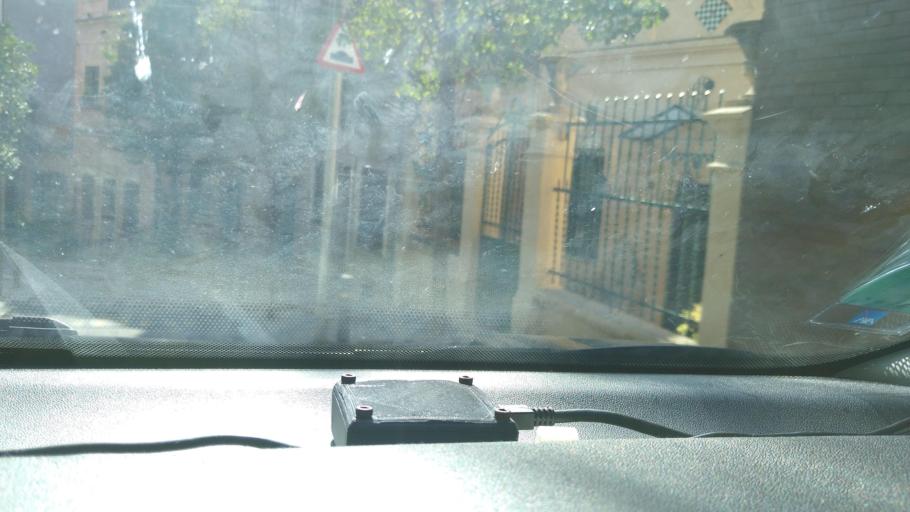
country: ES
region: Catalonia
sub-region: Provincia de Barcelona
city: Sant Andreu de Palomar
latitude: 41.4505
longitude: 2.1897
